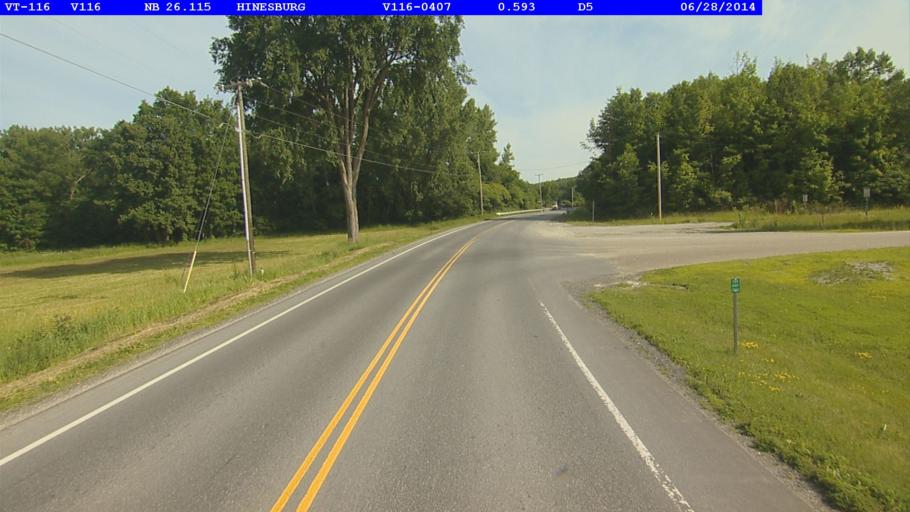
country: US
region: Vermont
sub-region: Chittenden County
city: Hinesburg
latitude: 44.2886
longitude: -73.0700
